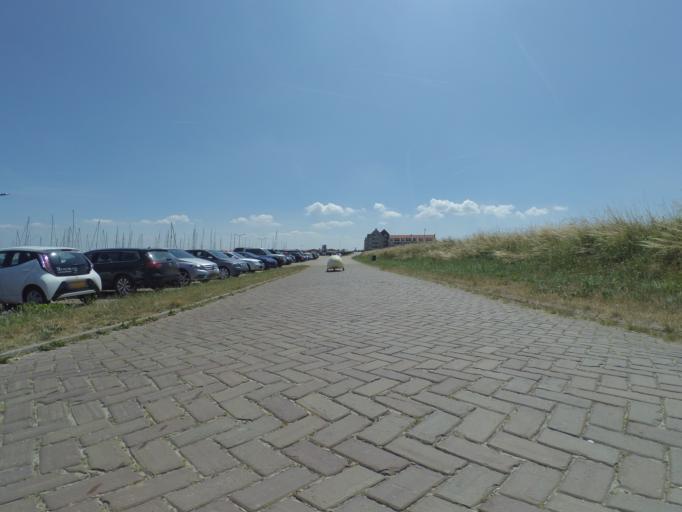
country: NL
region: Zeeland
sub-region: Schouwen-Duiveland
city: Bruinisse
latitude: 51.6046
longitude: 4.1050
